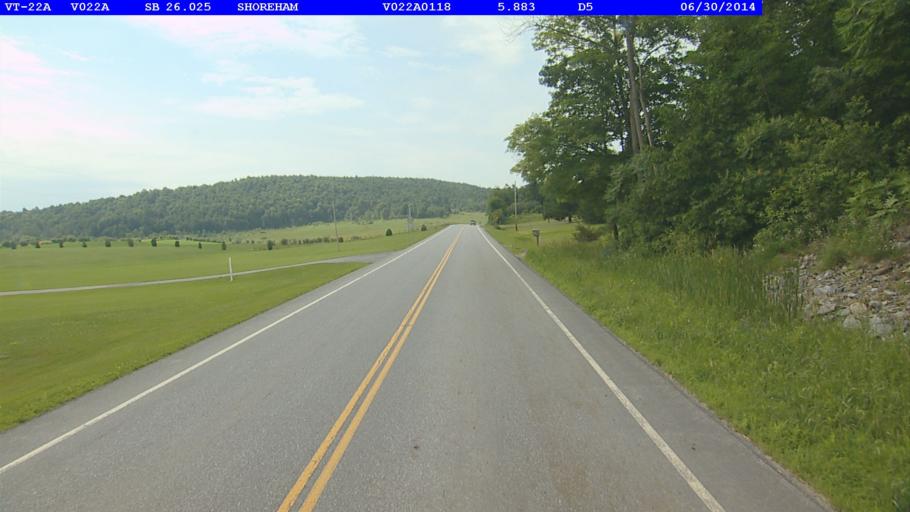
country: US
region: New York
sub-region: Essex County
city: Ticonderoga
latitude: 43.9338
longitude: -73.3098
